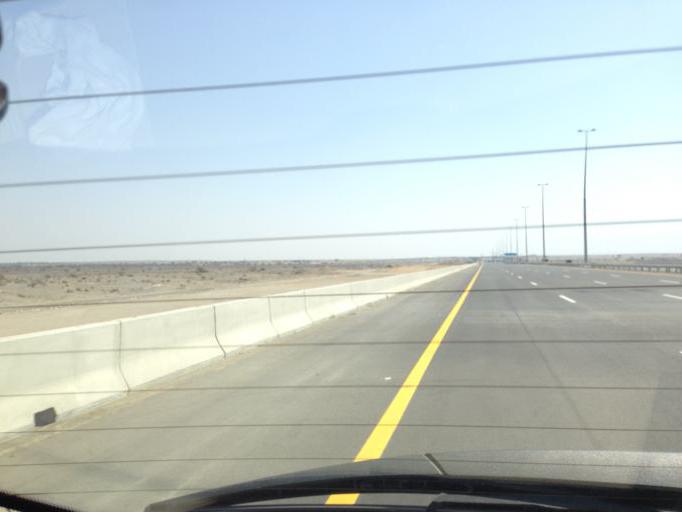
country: OM
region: Al Batinah
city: Rustaq
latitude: 23.5356
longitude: 57.5454
